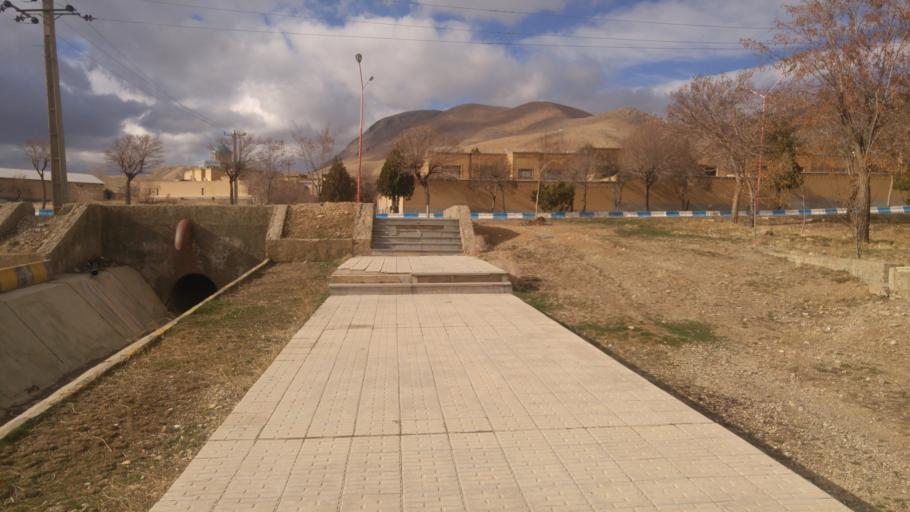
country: IR
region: Markazi
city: Shazand
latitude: 34.0458
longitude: 49.4177
